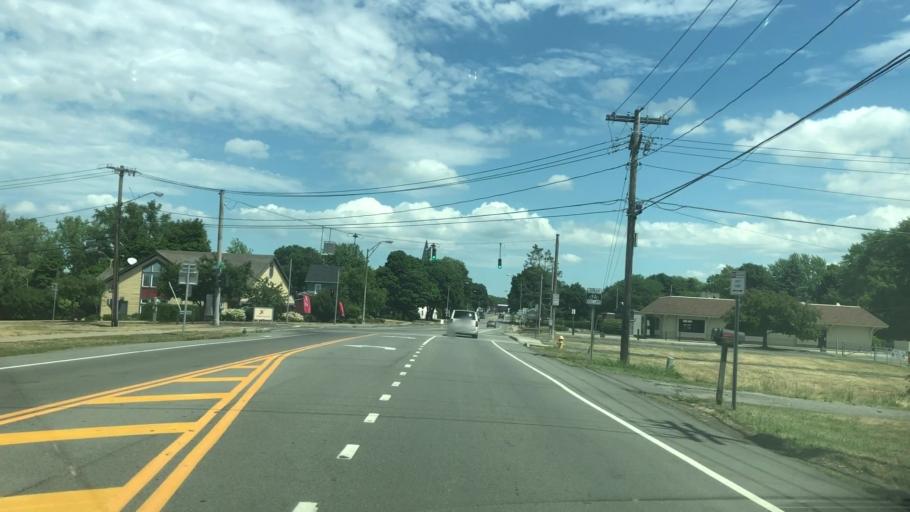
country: US
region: New York
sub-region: Monroe County
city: Webster
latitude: 43.2112
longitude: -77.4388
